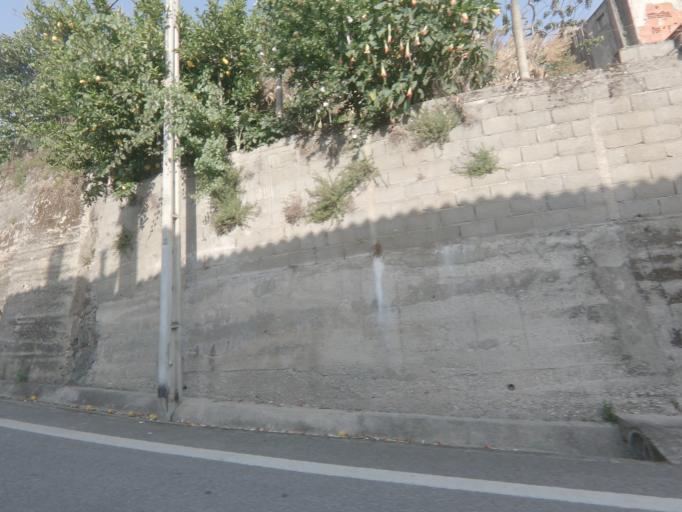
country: PT
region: Viseu
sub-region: Tabuaco
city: Tabuaco
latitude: 41.1319
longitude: -7.5338
